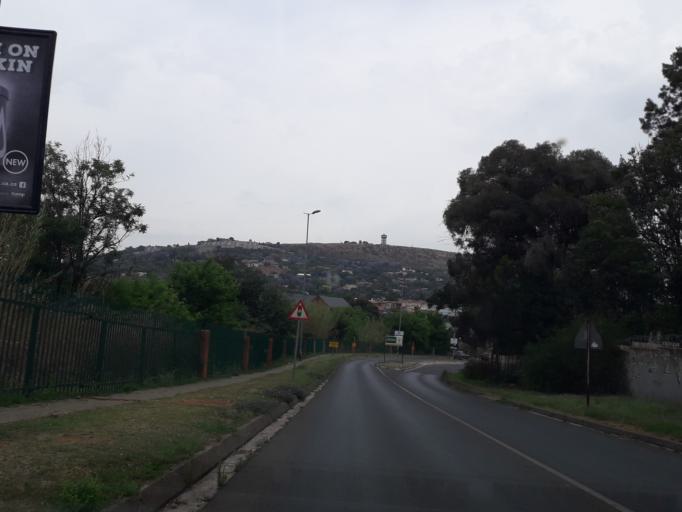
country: ZA
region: Gauteng
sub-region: City of Johannesburg Metropolitan Municipality
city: Johannesburg
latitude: -26.1286
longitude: 27.9793
